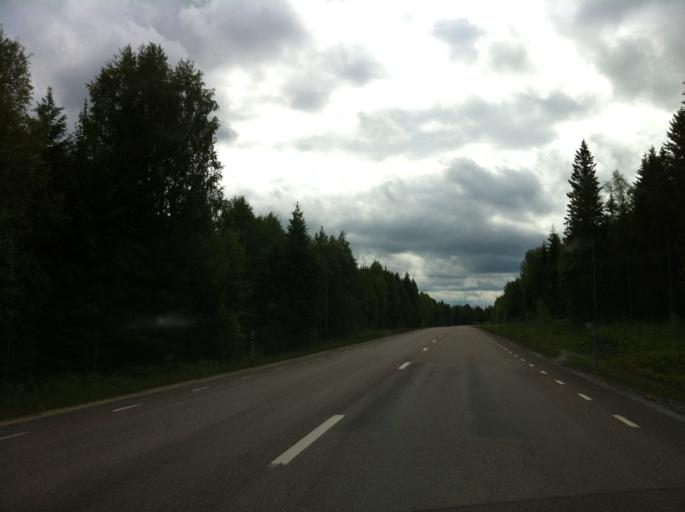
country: SE
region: Vaermland
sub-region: Sunne Kommun
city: Sunne
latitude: 59.7669
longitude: 13.1051
